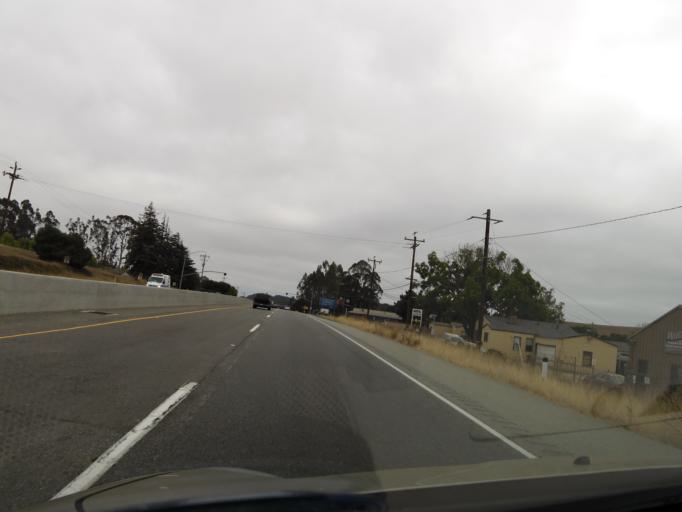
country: US
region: California
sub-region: Monterey County
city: Prunedale
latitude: 36.7775
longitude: -121.6697
